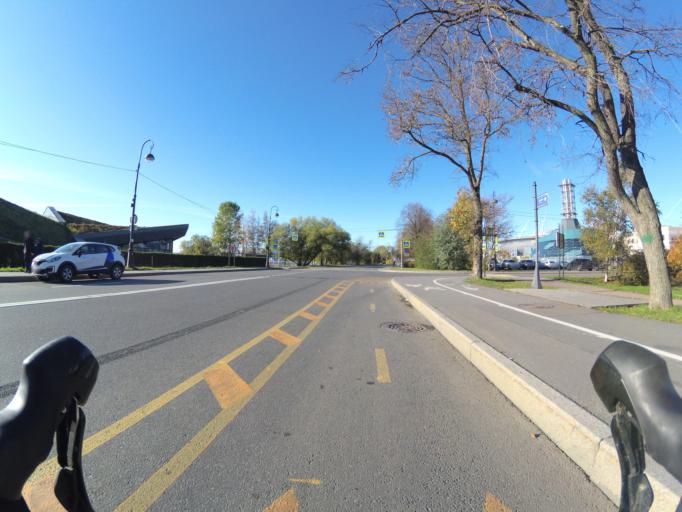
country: RU
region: St.-Petersburg
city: Staraya Derevnya
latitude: 59.9692
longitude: 30.2320
